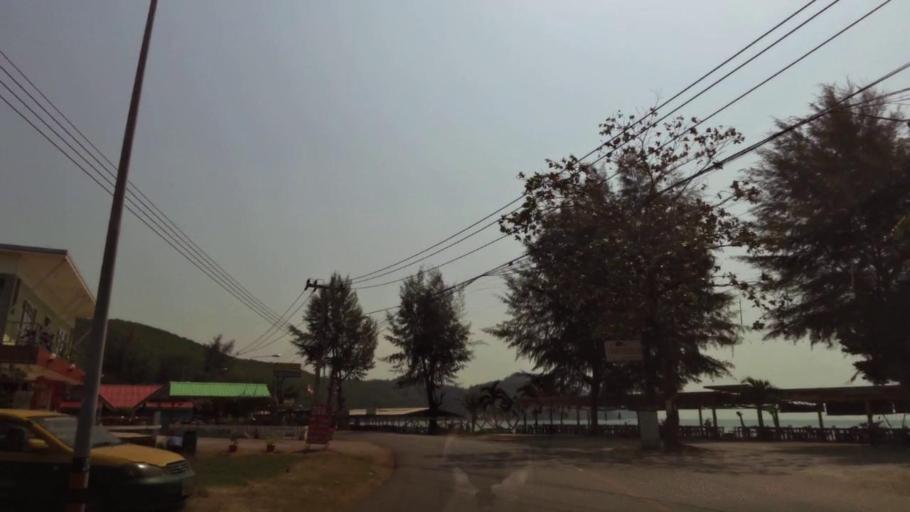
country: TH
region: Chanthaburi
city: Tha Mai
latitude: 12.5334
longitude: 101.9423
